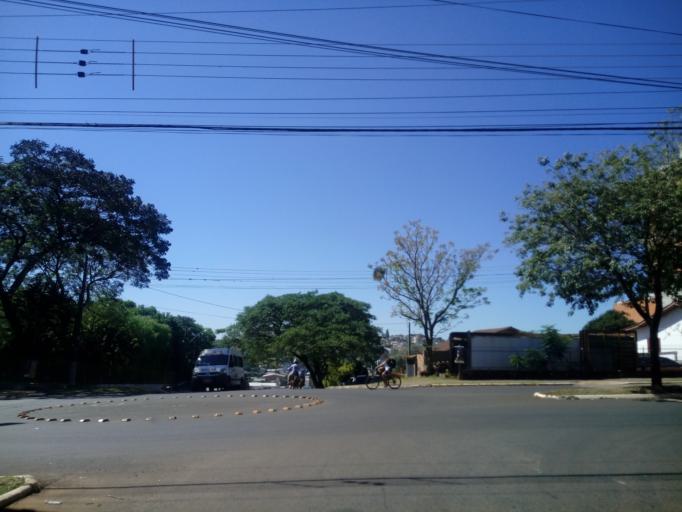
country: BR
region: Santa Catarina
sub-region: Chapeco
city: Chapeco
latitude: -27.1112
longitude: -52.6106
